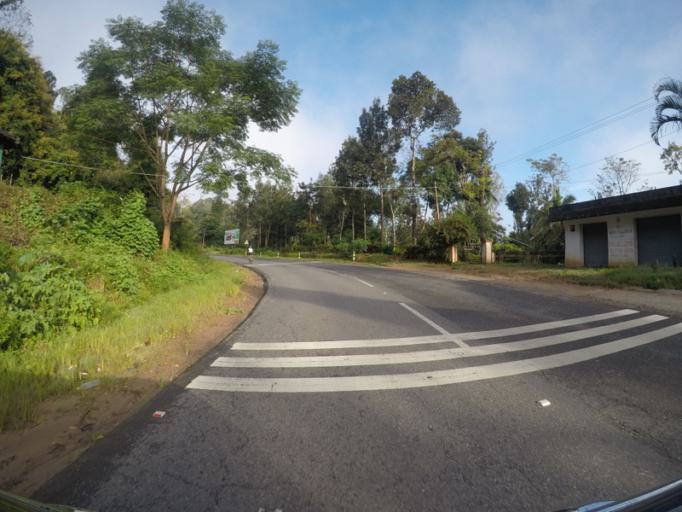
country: IN
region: Karnataka
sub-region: Kodagu
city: Suntikoppa
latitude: 12.4396
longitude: 75.7962
